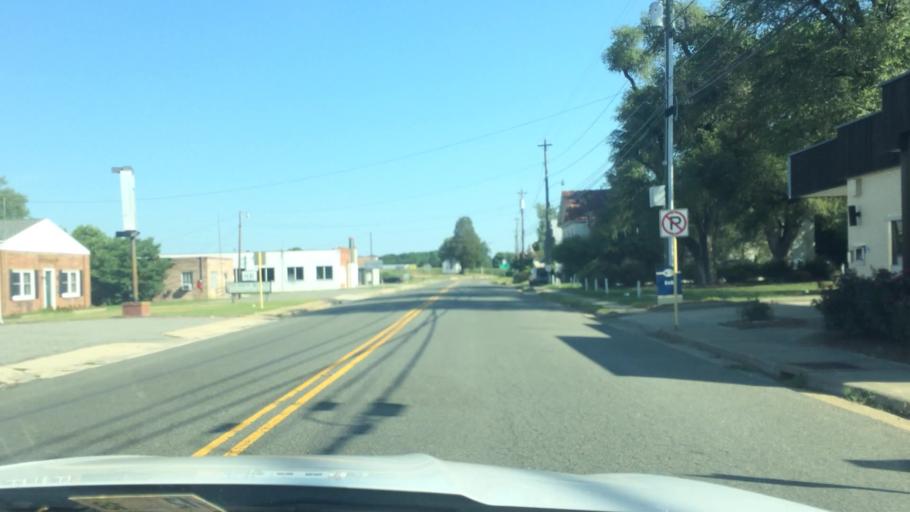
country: US
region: Virginia
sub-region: Lancaster County
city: Lancaster
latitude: 37.7779
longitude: -76.5137
